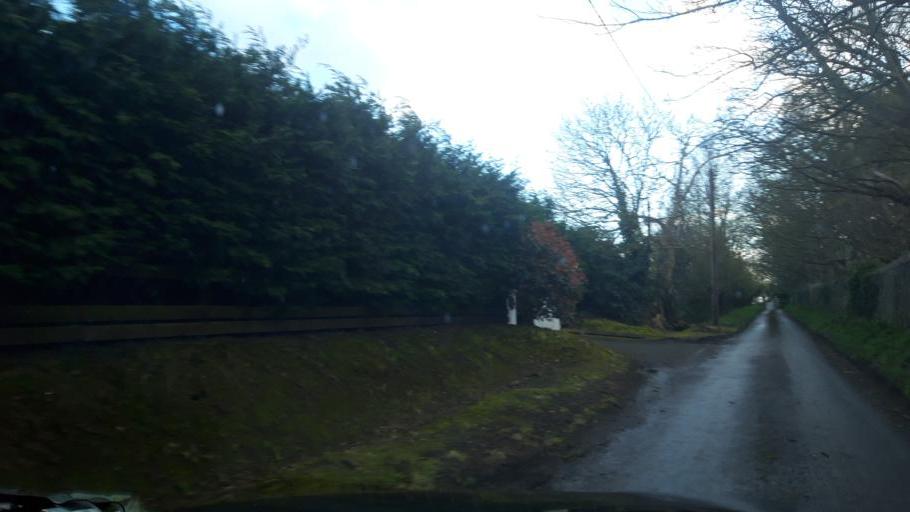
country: IE
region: Leinster
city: Donabate
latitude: 53.4732
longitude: -6.1703
